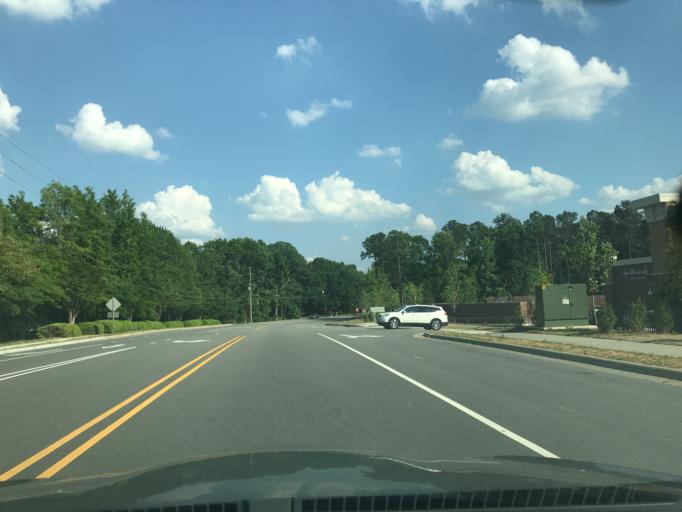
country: US
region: North Carolina
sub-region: Wake County
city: Wake Forest
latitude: 35.9022
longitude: -78.6025
